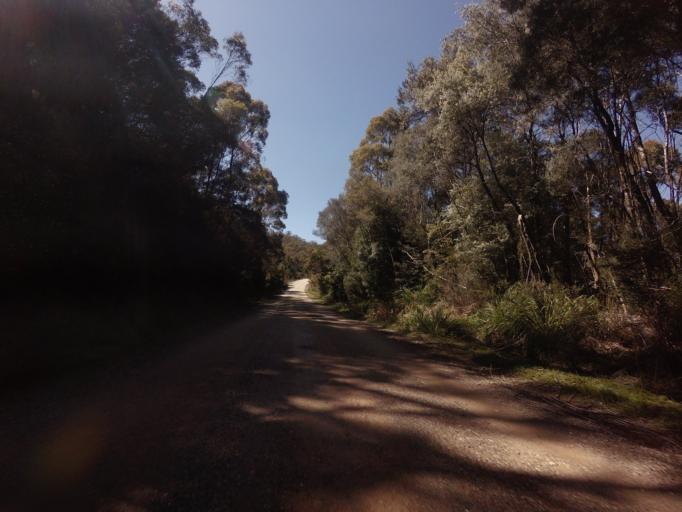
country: AU
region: Tasmania
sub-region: Huon Valley
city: Geeveston
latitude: -43.0090
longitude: 146.3610
